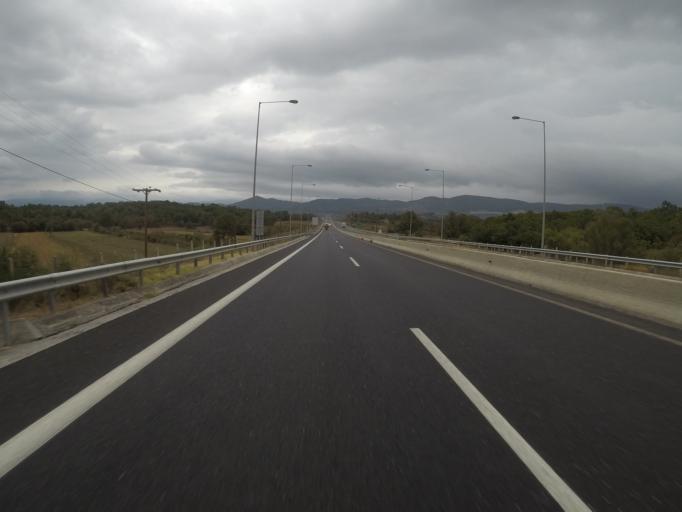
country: GR
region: Peloponnese
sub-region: Nomos Arkadias
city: Megalopoli
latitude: 37.3664
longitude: 22.1530
